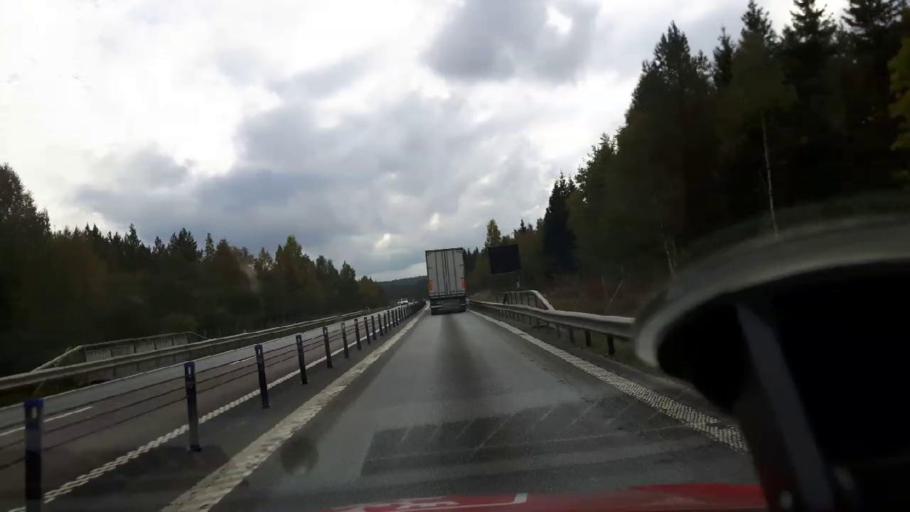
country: SE
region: Gaevleborg
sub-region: Gavle Kommun
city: Norrsundet
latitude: 60.9111
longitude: 17.0142
